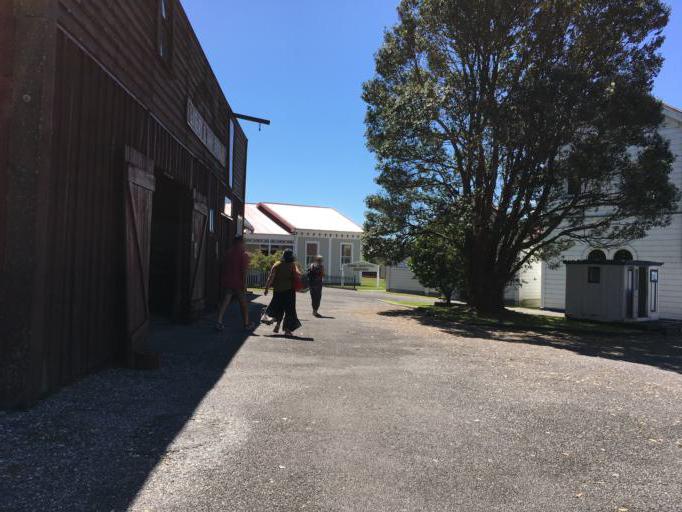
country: NZ
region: West Coast
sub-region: Grey District
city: Greymouth
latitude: -42.5353
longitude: 171.1815
